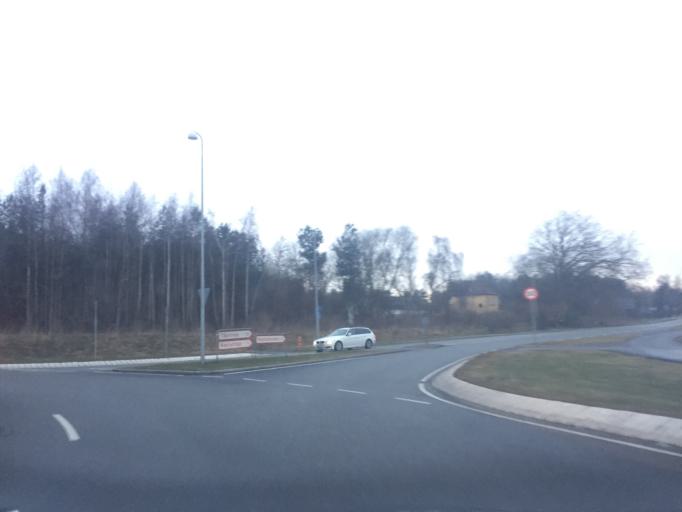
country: DK
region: Zealand
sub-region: Solrod Kommune
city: Solrod Strand
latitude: 55.5467
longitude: 12.2143
